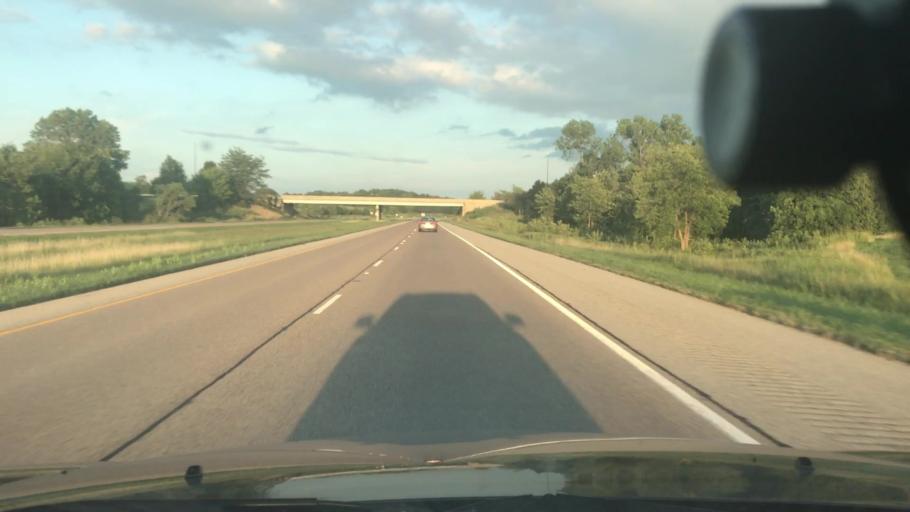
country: US
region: Illinois
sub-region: Clinton County
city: Albers
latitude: 38.5011
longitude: -89.6149
